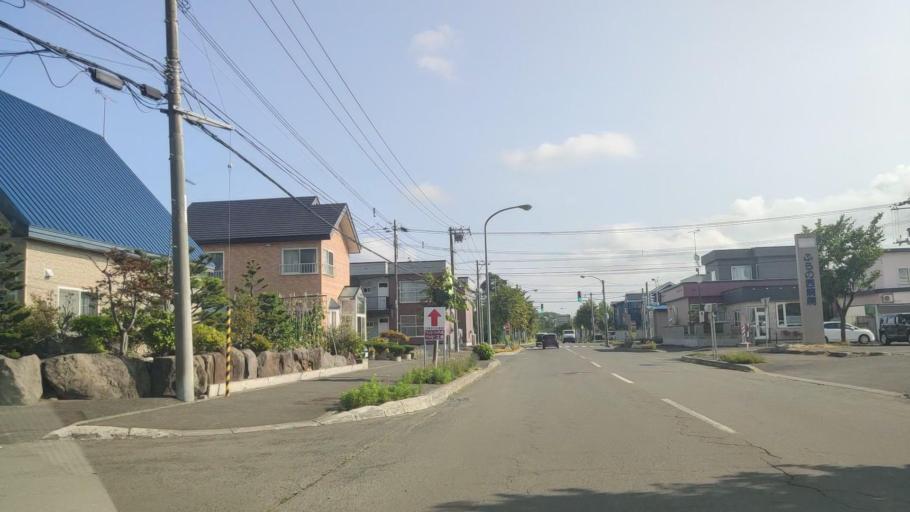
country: JP
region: Hokkaido
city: Shimo-furano
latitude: 43.3508
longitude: 142.3789
